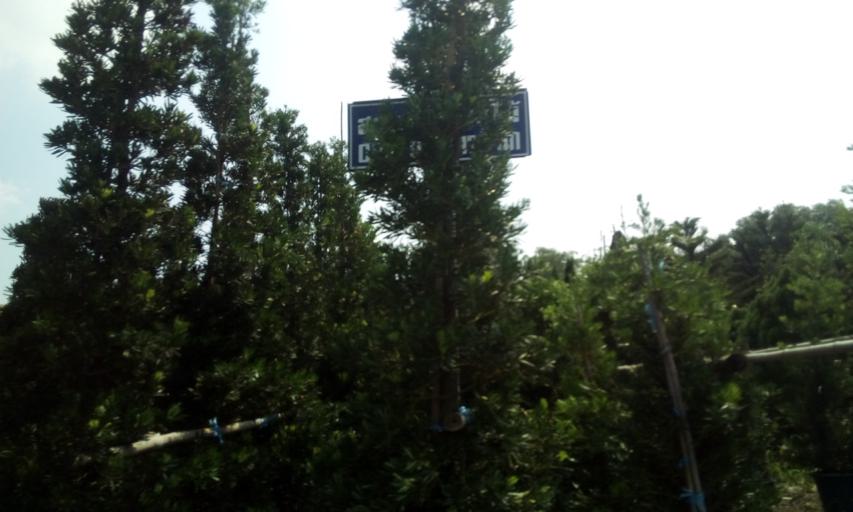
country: TH
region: Nakhon Nayok
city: Ongkharak
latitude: 14.1274
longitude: 100.9450
